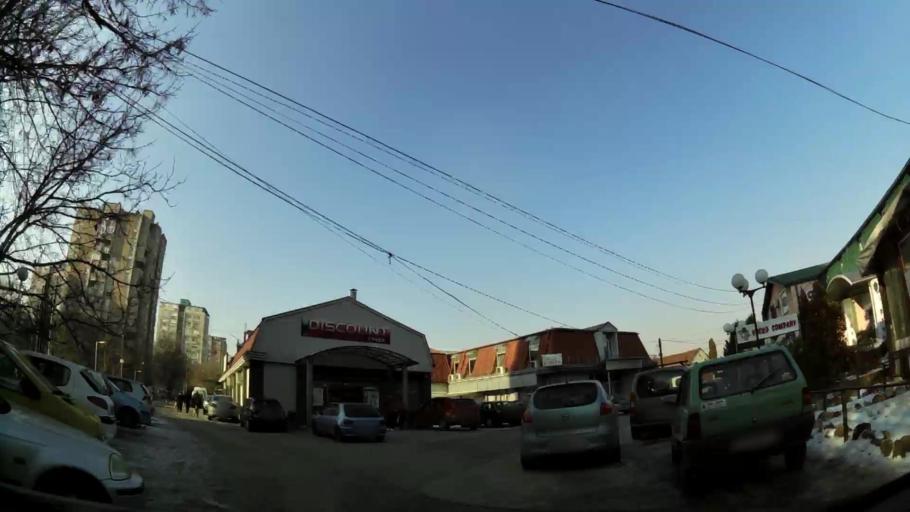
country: MK
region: Karpos
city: Skopje
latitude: 41.9895
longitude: 21.4553
